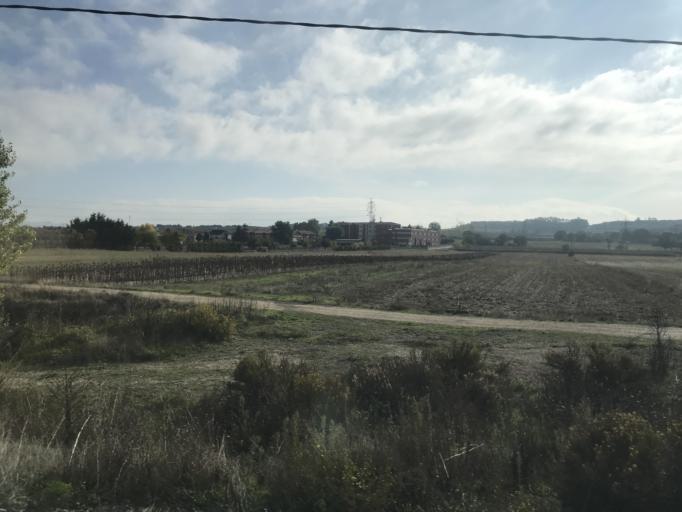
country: ES
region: Castille and Leon
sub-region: Provincia de Burgos
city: Miranda de Ebro
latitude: 42.6779
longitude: -2.9767
